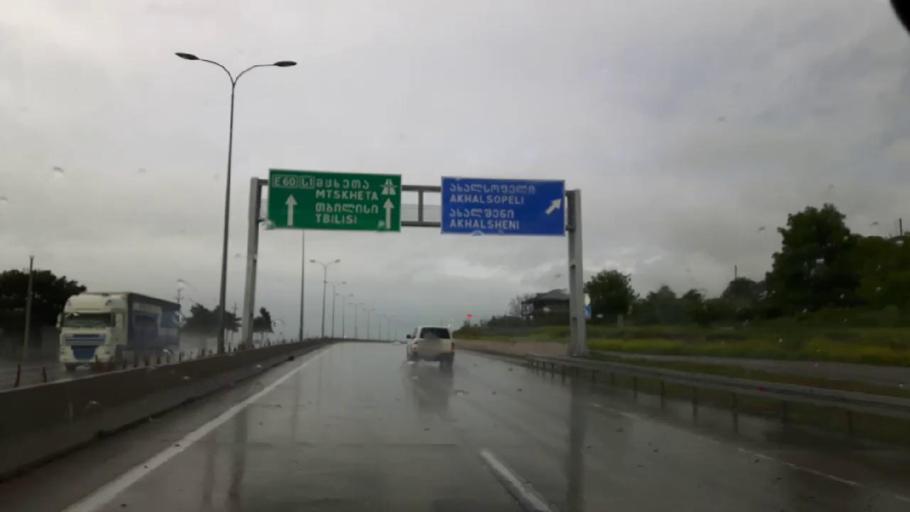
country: GE
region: Shida Kartli
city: Gori
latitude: 42.0264
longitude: 44.1991
